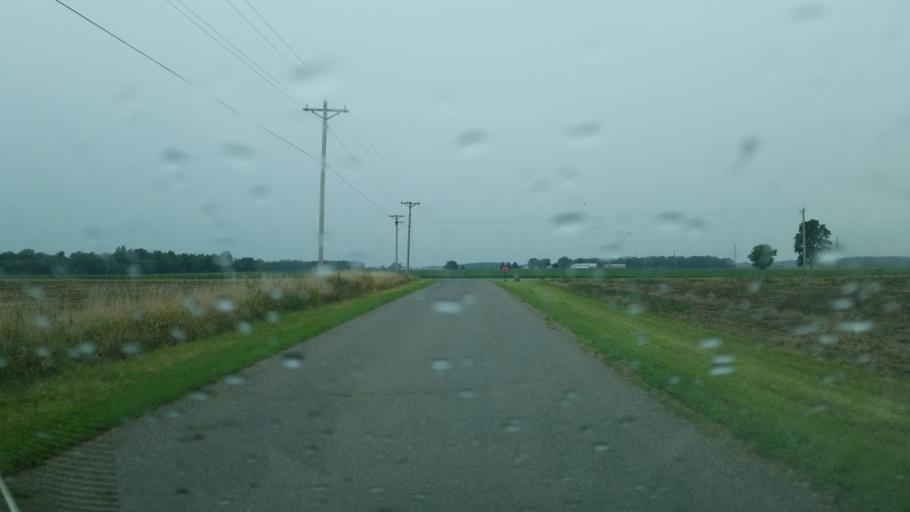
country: US
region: Ohio
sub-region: Huron County
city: Willard
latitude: 41.0093
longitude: -82.8139
